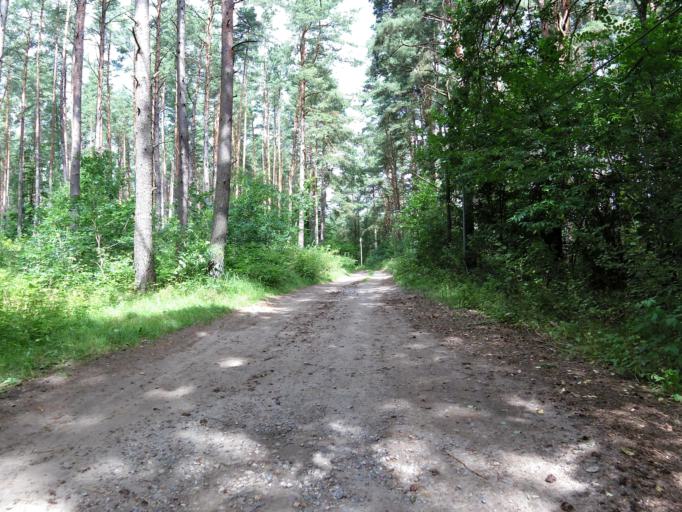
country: DE
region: Brandenburg
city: Lychen
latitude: 53.2176
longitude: 13.2761
